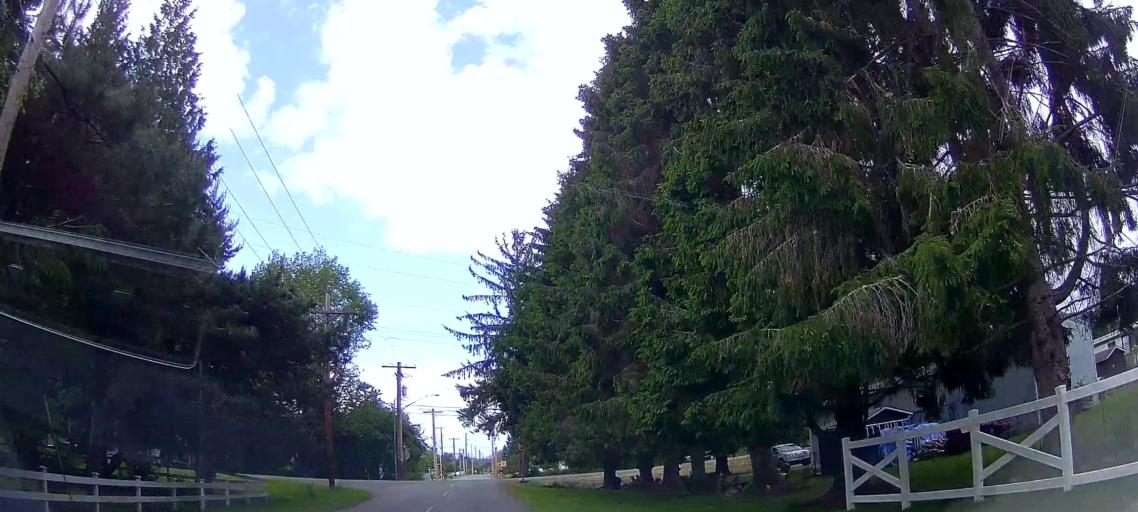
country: US
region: Washington
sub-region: Skagit County
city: Sedro-Woolley
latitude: 48.5043
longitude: -122.2098
